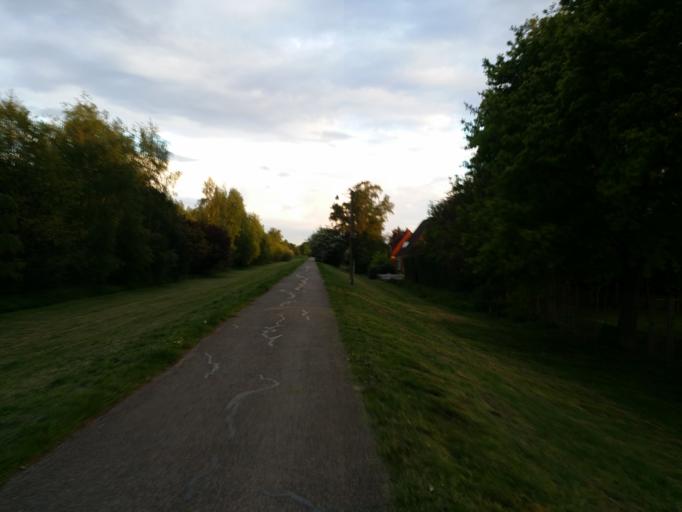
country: DE
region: Lower Saxony
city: Stuhr
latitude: 53.0594
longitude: 8.7681
